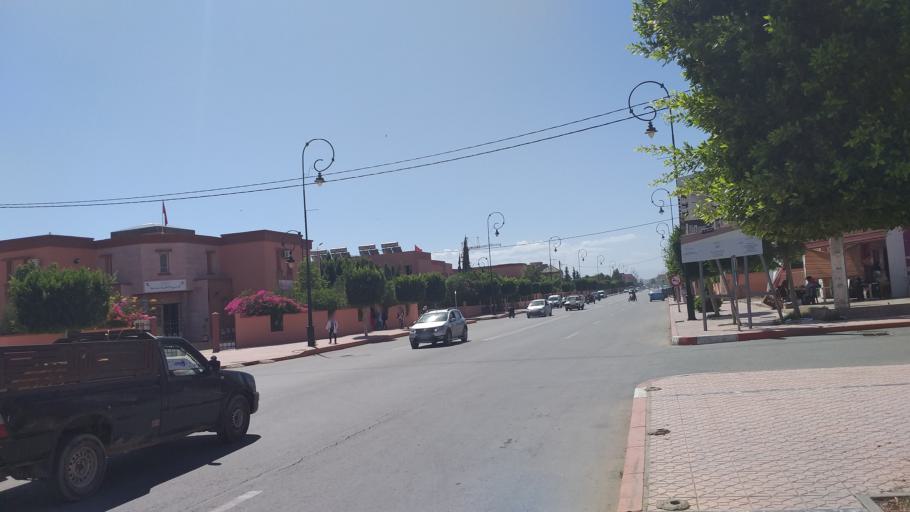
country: MA
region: Marrakech-Tensift-Al Haouz
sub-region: Chichaoua
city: Chichaoua
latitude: 31.5404
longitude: -8.7675
